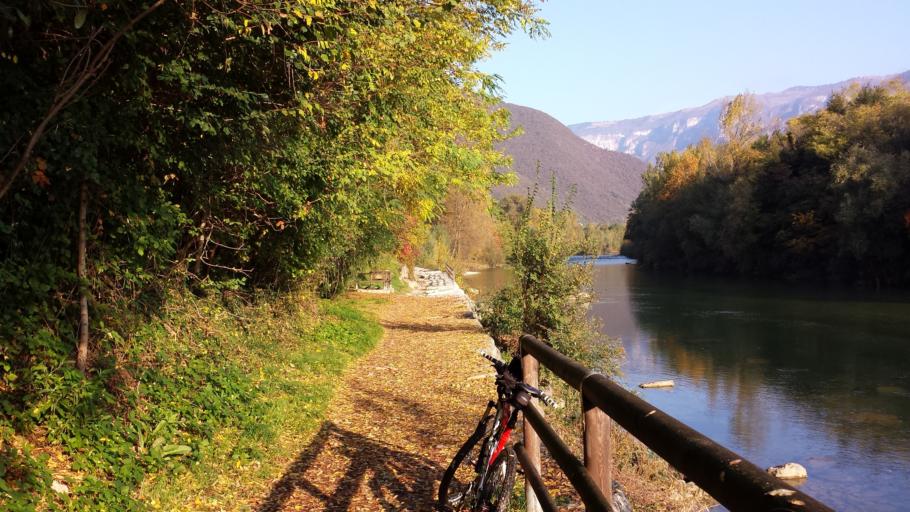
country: IT
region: Veneto
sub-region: Provincia di Vicenza
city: Campese
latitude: 45.7911
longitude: 11.7162
